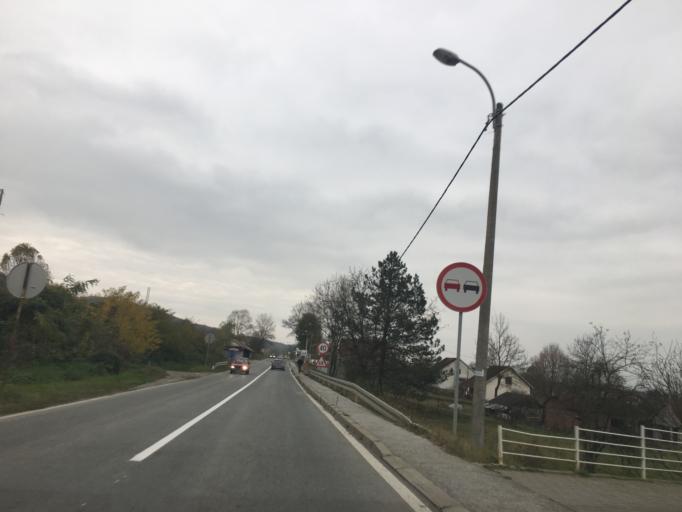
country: RS
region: Central Serbia
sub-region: Raski Okrug
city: Kraljevo
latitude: 43.7272
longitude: 20.7573
